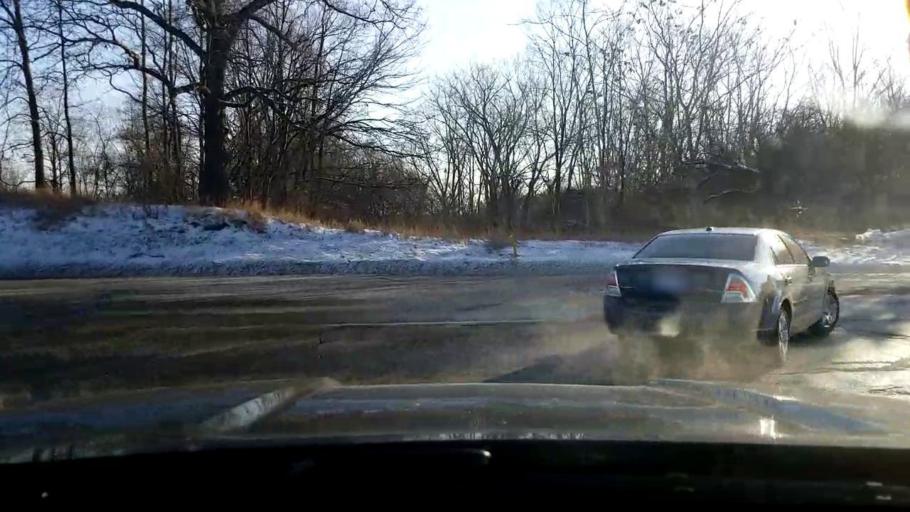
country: US
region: Michigan
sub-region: Jackson County
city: Jackson
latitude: 42.2839
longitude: -84.3845
